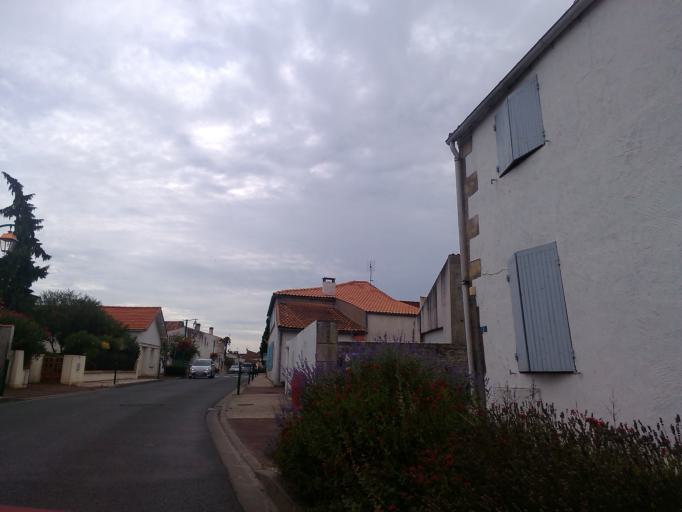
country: FR
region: Poitou-Charentes
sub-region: Departement de la Charente-Maritime
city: Breuillet
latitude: 45.6938
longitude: -1.0516
